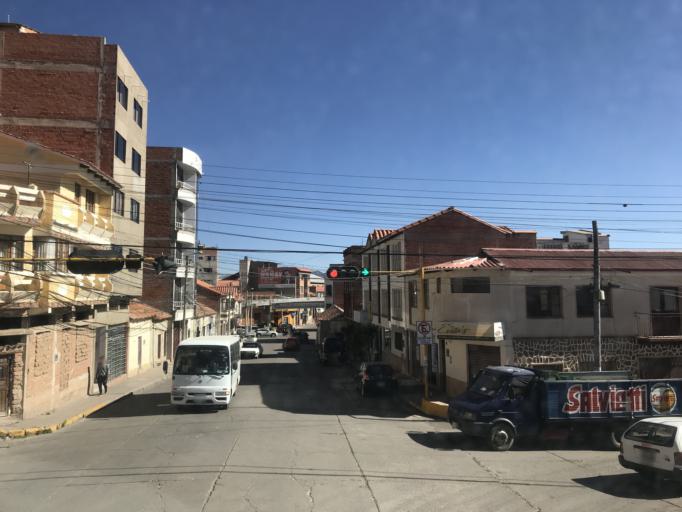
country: BO
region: Chuquisaca
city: Sucre
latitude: -19.0431
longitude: -65.2488
